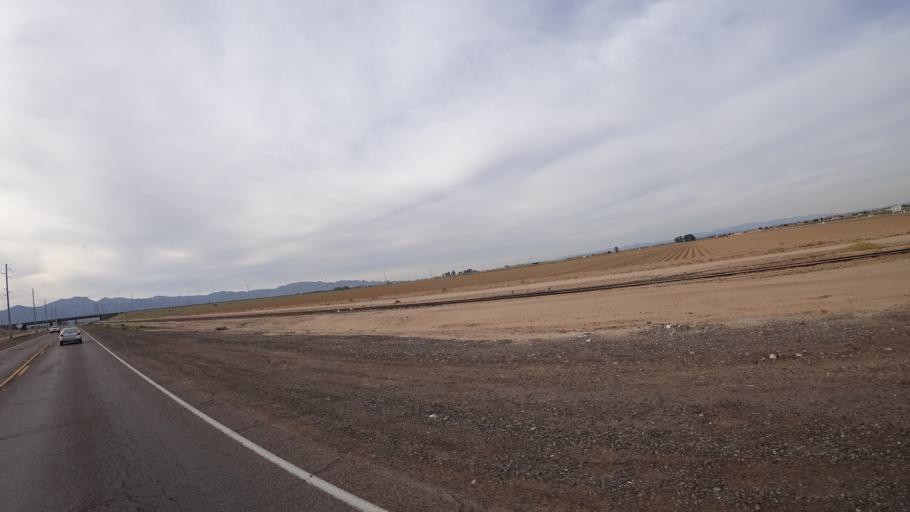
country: US
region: Arizona
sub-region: Maricopa County
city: Citrus Park
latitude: 33.5663
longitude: -112.4101
